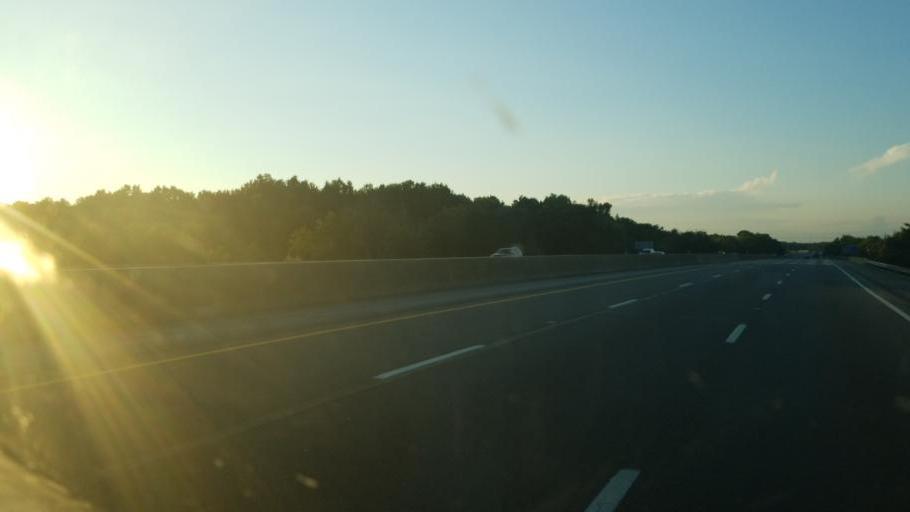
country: US
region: Ohio
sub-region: Trumbull County
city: Newton Falls
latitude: 41.2019
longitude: -80.9468
